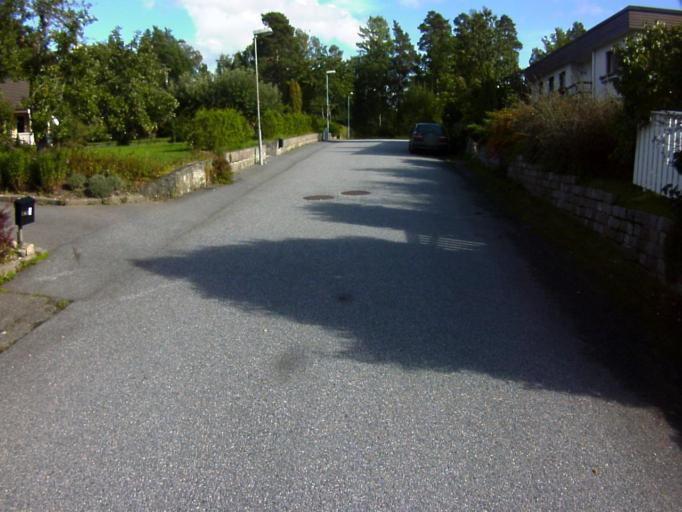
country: SE
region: Soedermanland
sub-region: Eskilstuna Kommun
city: Eskilstuna
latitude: 59.3916
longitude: 16.5424
